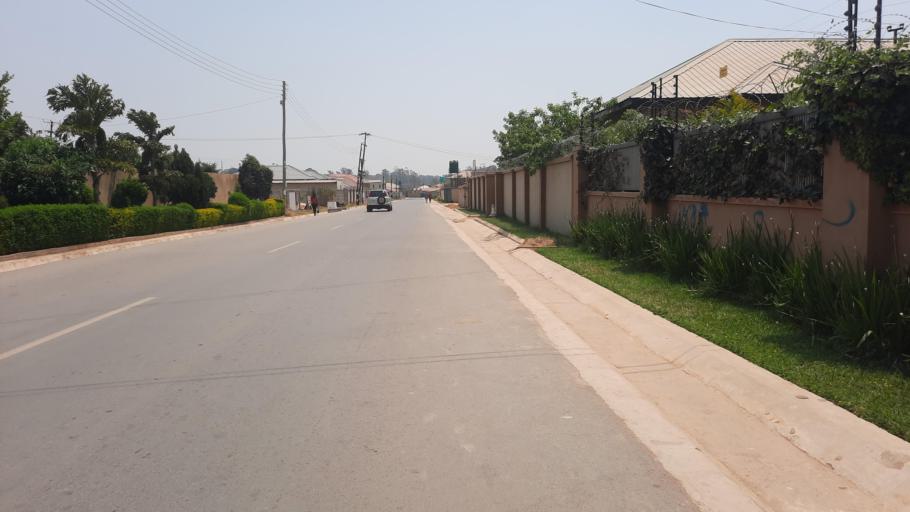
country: ZM
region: Lusaka
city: Lusaka
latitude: -15.3950
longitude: 28.3844
